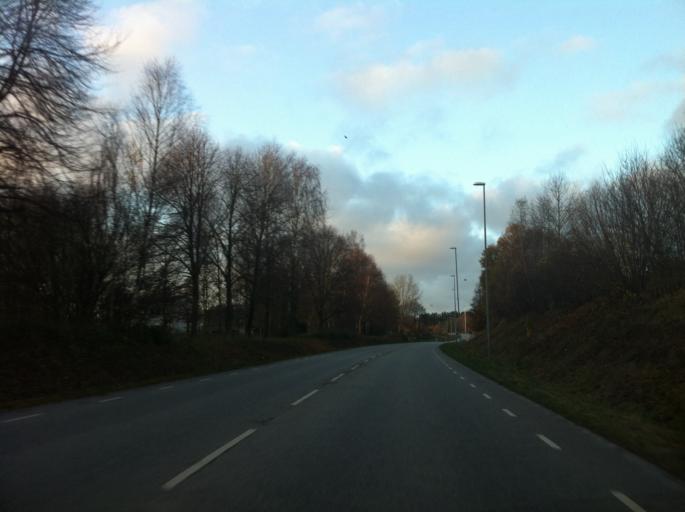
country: SE
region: Skane
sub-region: Hoors Kommun
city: Hoeoer
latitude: 55.9388
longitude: 13.5499
